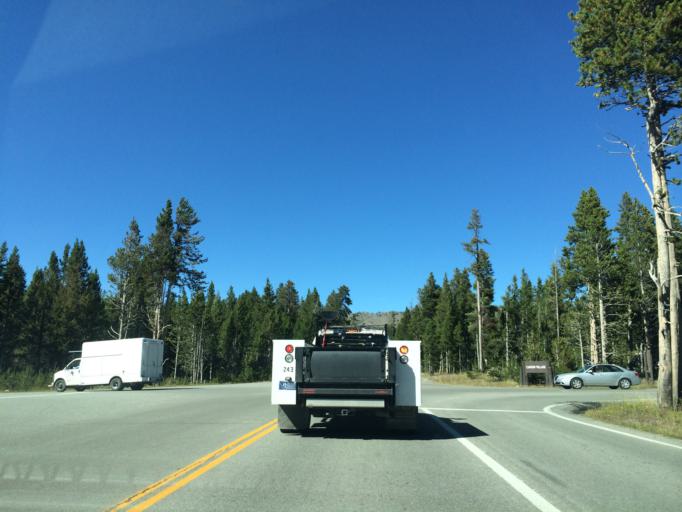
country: US
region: Montana
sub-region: Gallatin County
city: West Yellowstone
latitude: 44.7356
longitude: -110.4933
